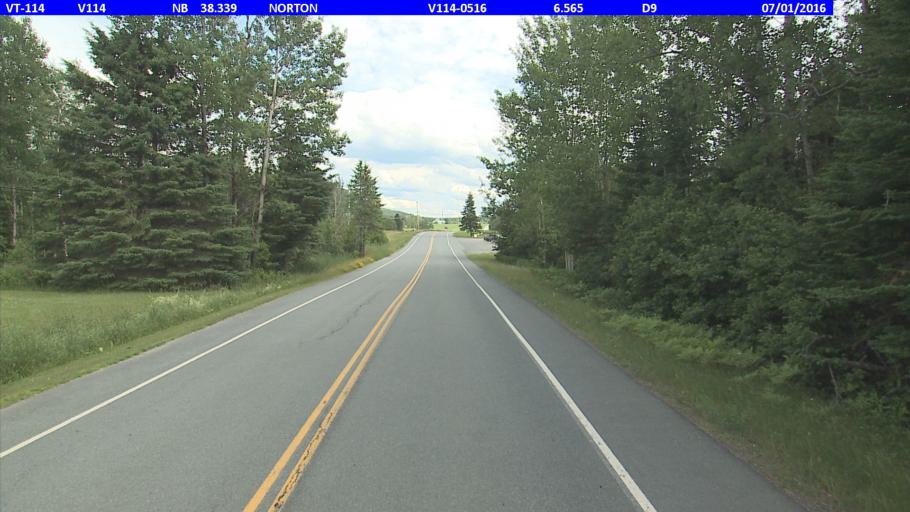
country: CA
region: Quebec
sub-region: Estrie
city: Coaticook
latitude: 45.0062
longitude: -71.7720
